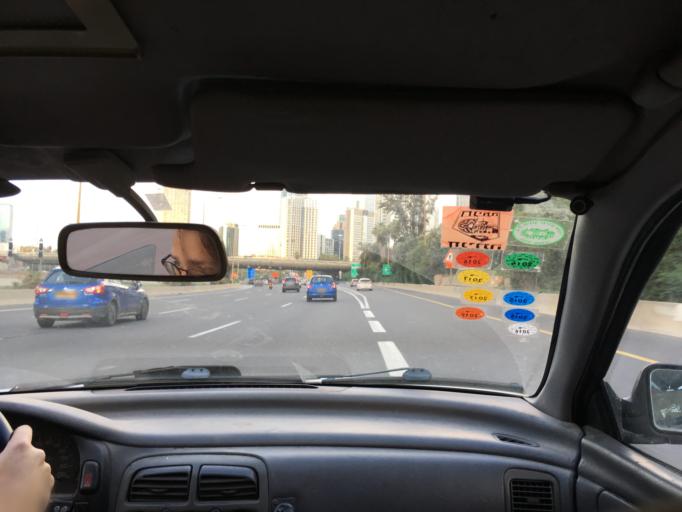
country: IL
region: Tel Aviv
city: Ramat Gan
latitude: 32.0785
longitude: 34.7964
